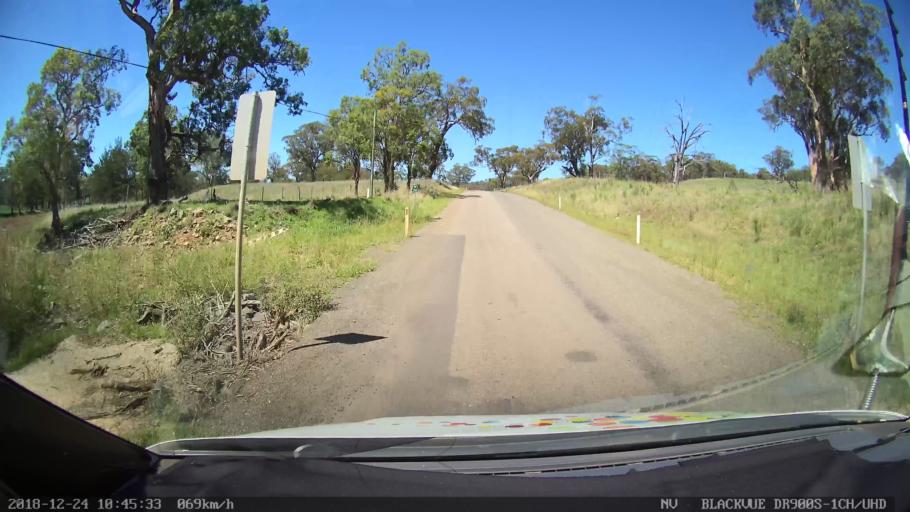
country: AU
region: New South Wales
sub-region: Upper Hunter Shire
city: Merriwa
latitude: -31.9040
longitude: 150.4349
